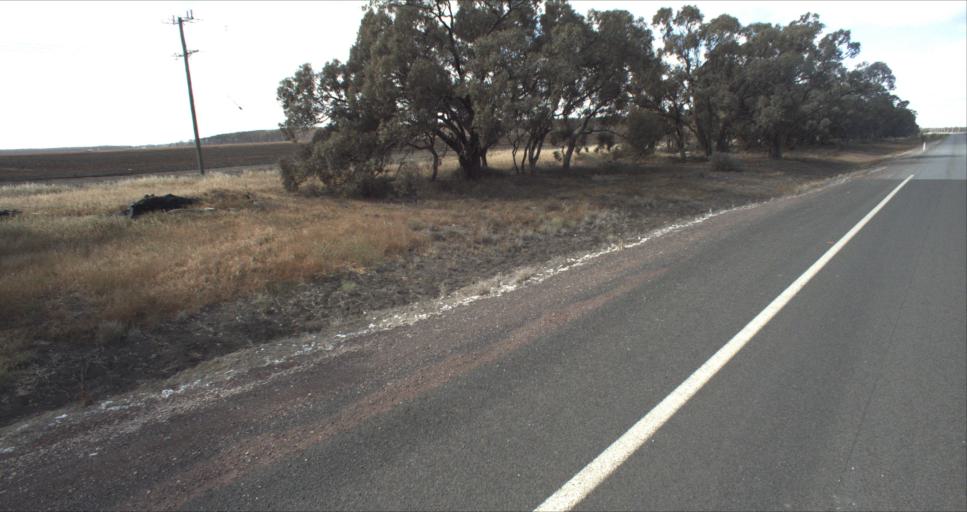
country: AU
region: New South Wales
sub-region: Murrumbidgee Shire
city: Darlington Point
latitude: -34.5753
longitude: 146.1663
